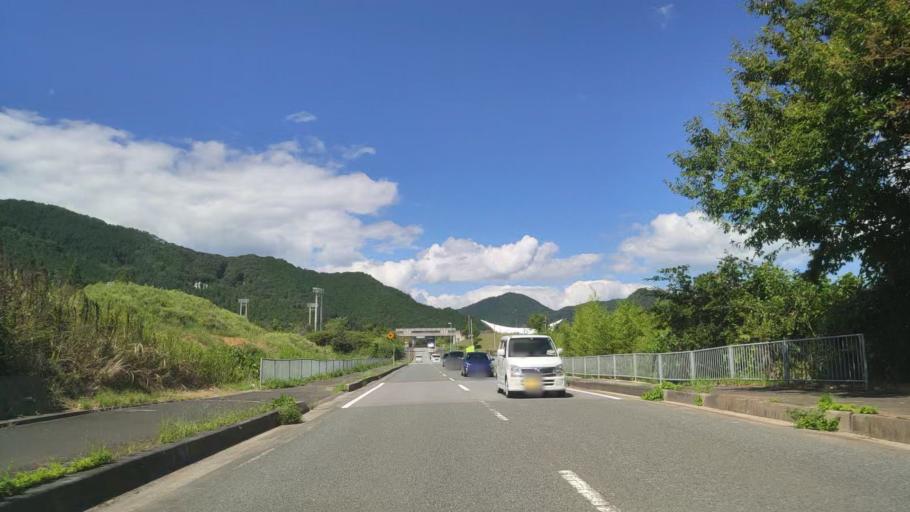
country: JP
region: Kyoto
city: Fukuchiyama
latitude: 35.2349
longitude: 135.1268
